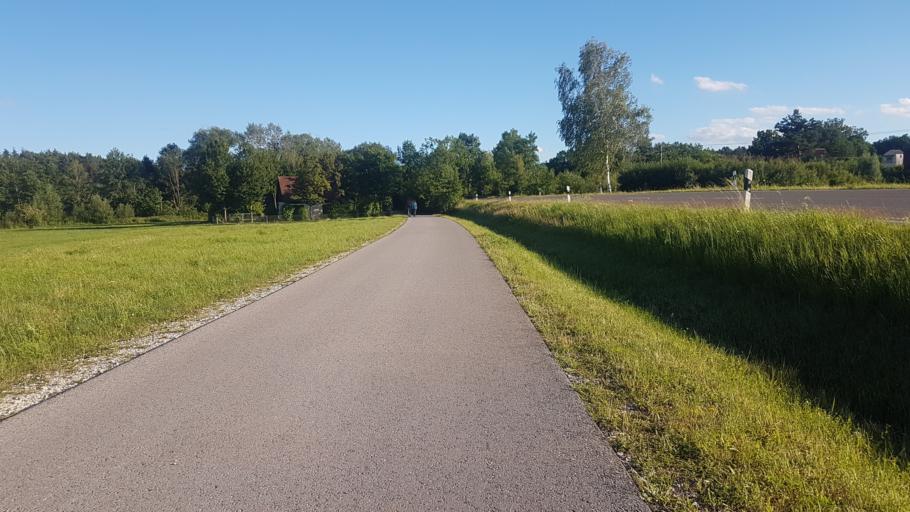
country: DE
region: Bavaria
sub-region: Regierungsbezirk Mittelfranken
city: Absberg
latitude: 49.1309
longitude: 10.8562
